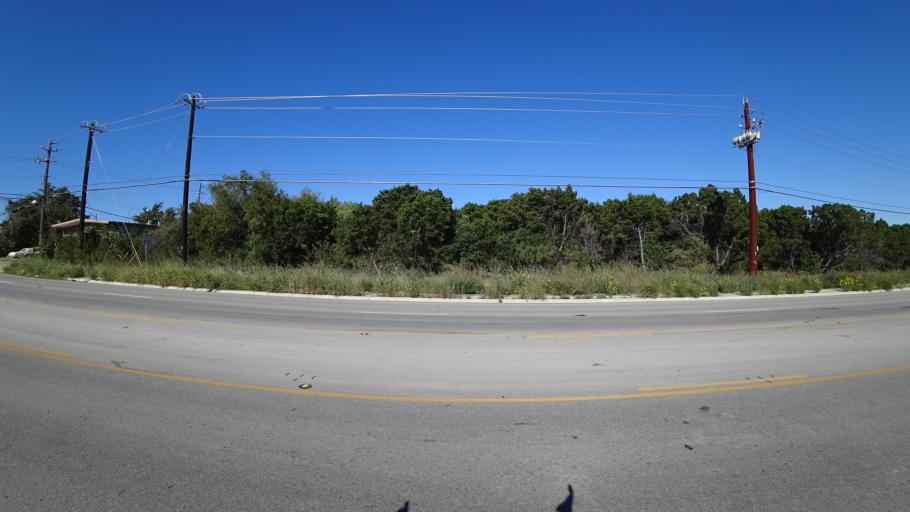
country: US
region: Texas
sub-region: Travis County
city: Austin
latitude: 30.3228
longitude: -97.6586
